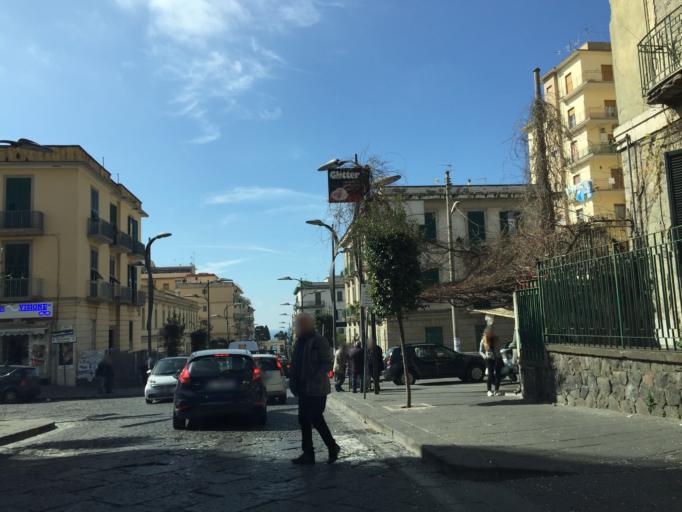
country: IT
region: Campania
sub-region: Provincia di Napoli
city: Ercolano
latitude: 40.8075
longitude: 14.3517
